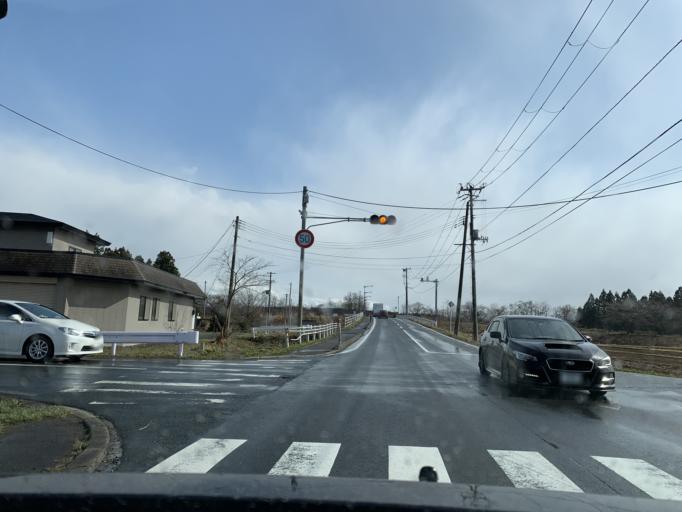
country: JP
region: Iwate
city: Kitakami
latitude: 39.2929
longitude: 141.0550
